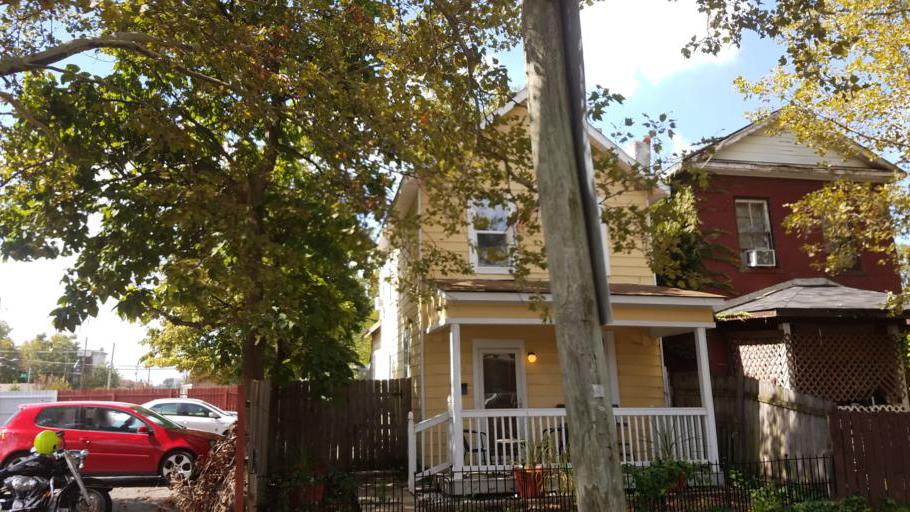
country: US
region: Ohio
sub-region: Franklin County
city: Columbus
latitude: 39.9577
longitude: -83.0128
